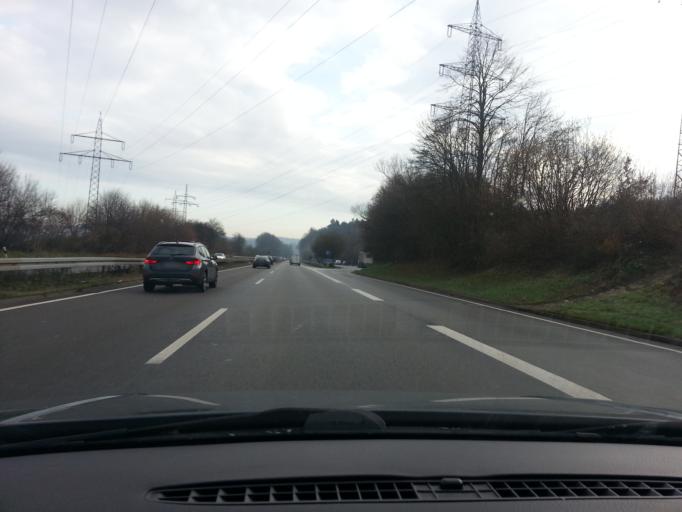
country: DE
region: Saarland
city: Kirkel
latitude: 49.3004
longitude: 7.2851
